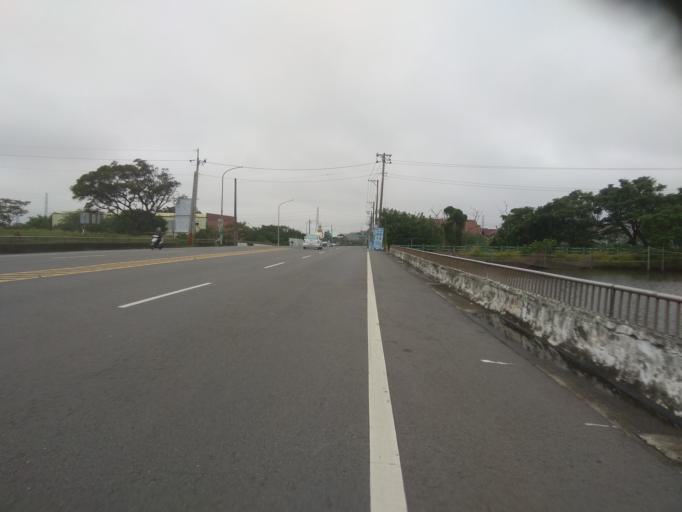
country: TW
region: Taiwan
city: Taoyuan City
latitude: 25.0123
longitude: 121.1344
